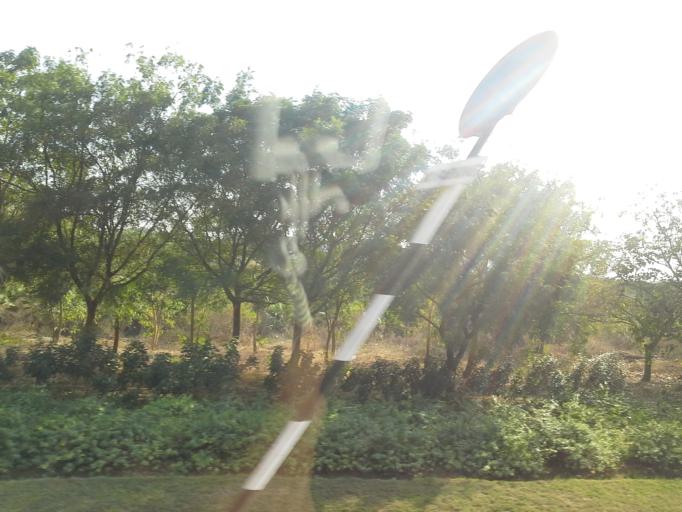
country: IN
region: Telangana
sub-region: Rangareddi
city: Balapur
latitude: 17.2406
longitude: 78.4208
